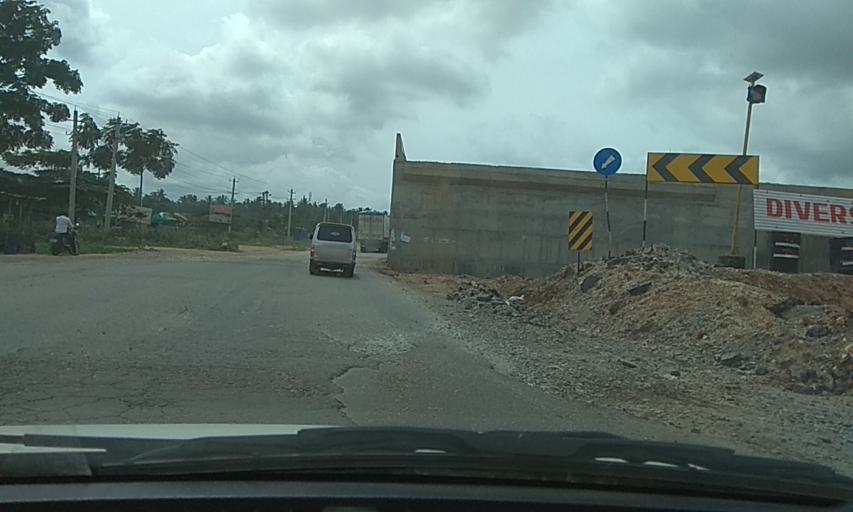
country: IN
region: Karnataka
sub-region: Davanagere
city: Mayakonda
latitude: 14.4258
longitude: 75.9737
